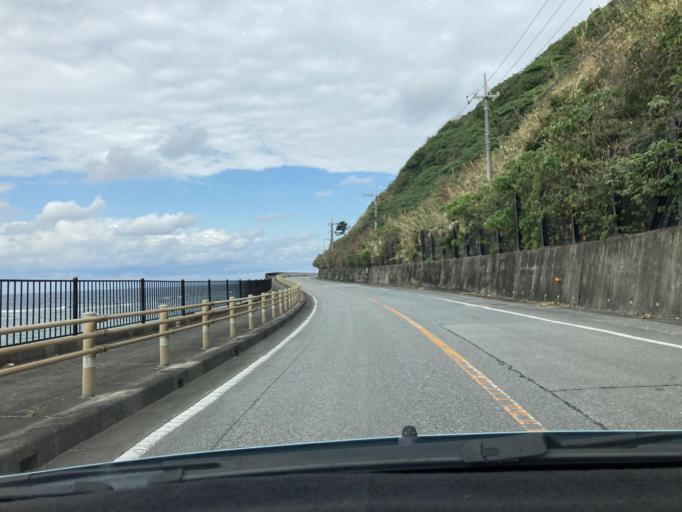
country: JP
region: Okinawa
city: Nago
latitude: 26.7896
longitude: 128.2241
